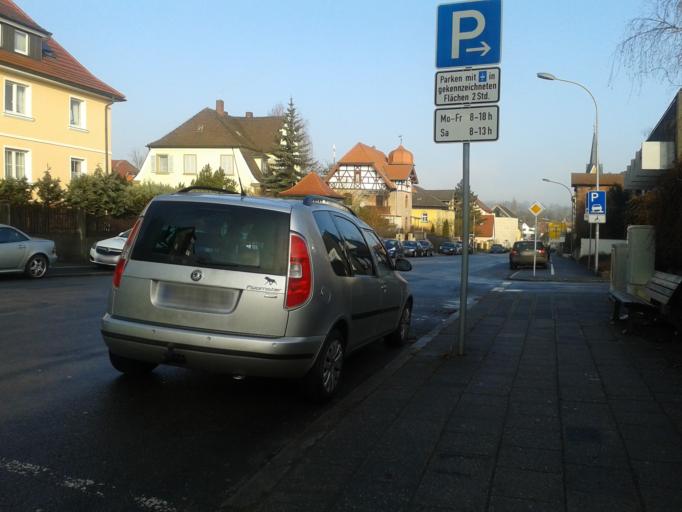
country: DE
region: Bavaria
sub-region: Regierungsbezirk Mittelfranken
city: Neustadt an der Aisch
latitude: 49.5759
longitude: 10.6056
